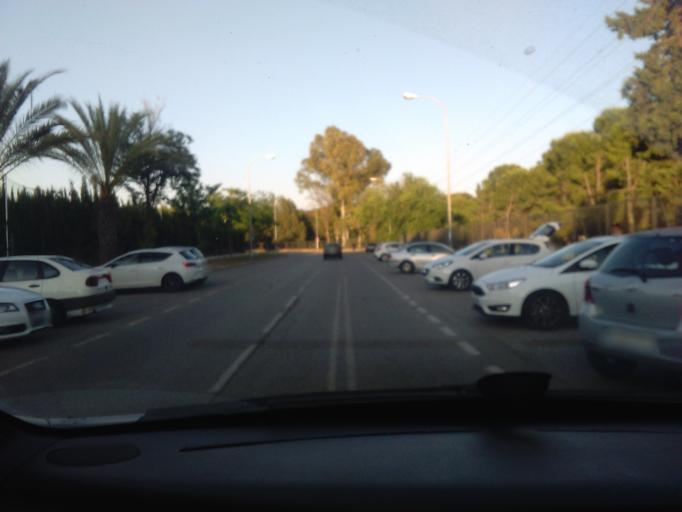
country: ES
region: Andalusia
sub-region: Provincia de Sevilla
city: Sevilla
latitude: 37.3970
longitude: -5.9414
